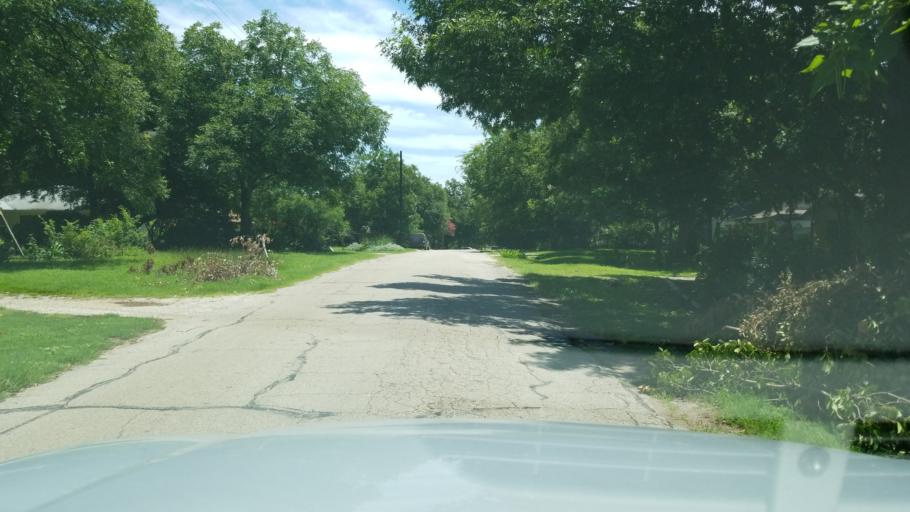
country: US
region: Texas
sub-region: Dallas County
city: Irving
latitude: 32.8042
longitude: -96.9154
